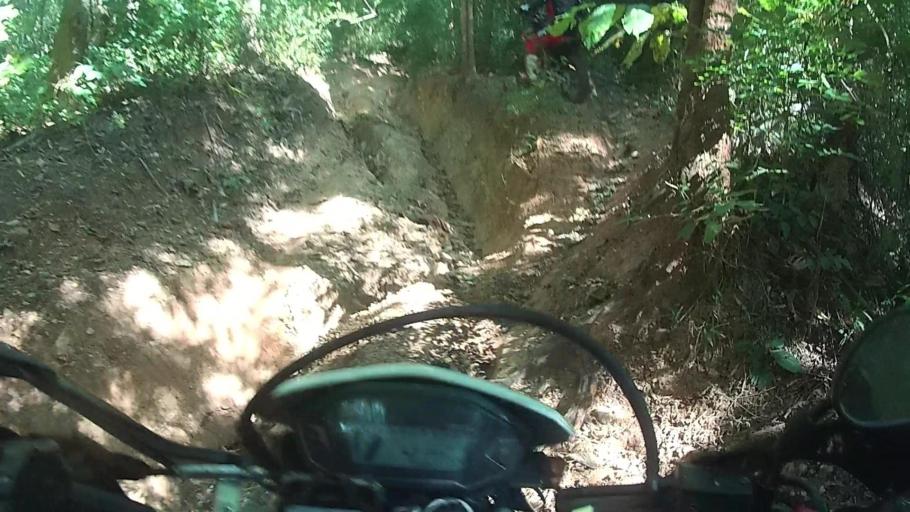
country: TH
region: Chiang Mai
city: Chiang Mai
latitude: 18.9212
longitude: 98.8931
